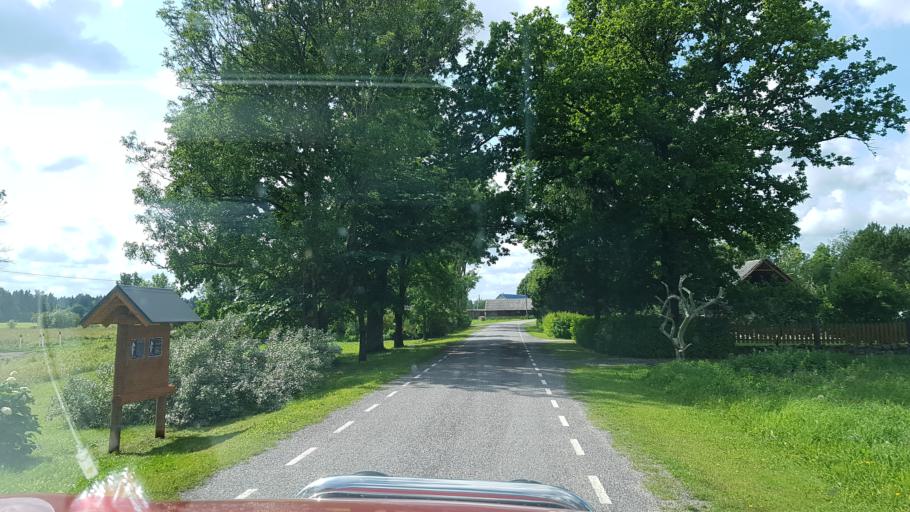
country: EE
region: Raplamaa
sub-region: Rapla vald
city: Rapla
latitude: 58.9675
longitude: 24.6229
